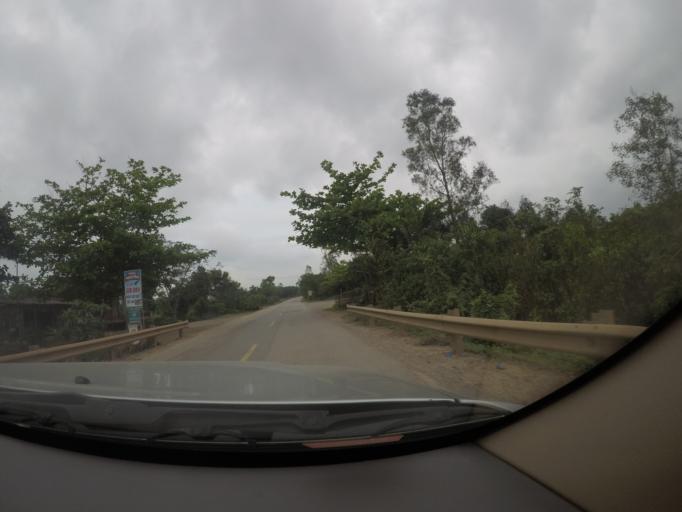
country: VN
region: Quang Binh
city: Kien Giang
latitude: 17.1447
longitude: 106.7614
